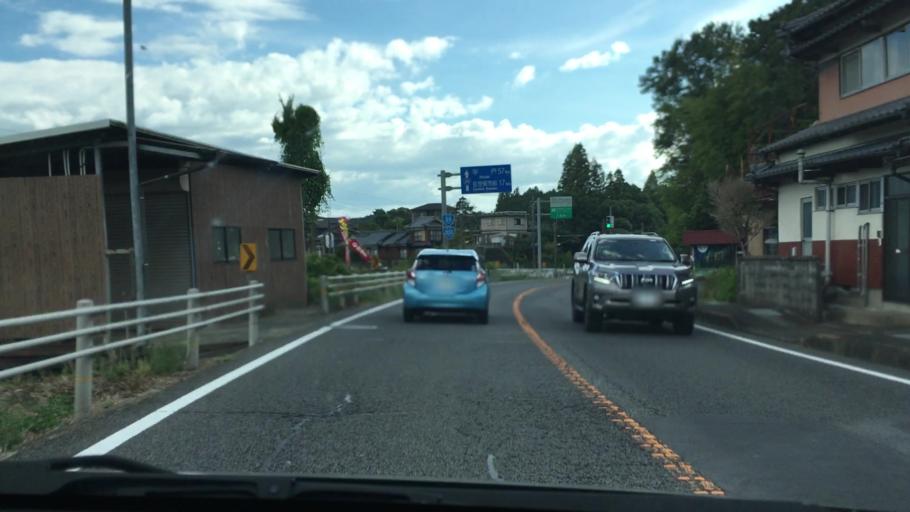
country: JP
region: Saga Prefecture
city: Imaricho-ko
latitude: 33.1768
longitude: 129.8515
